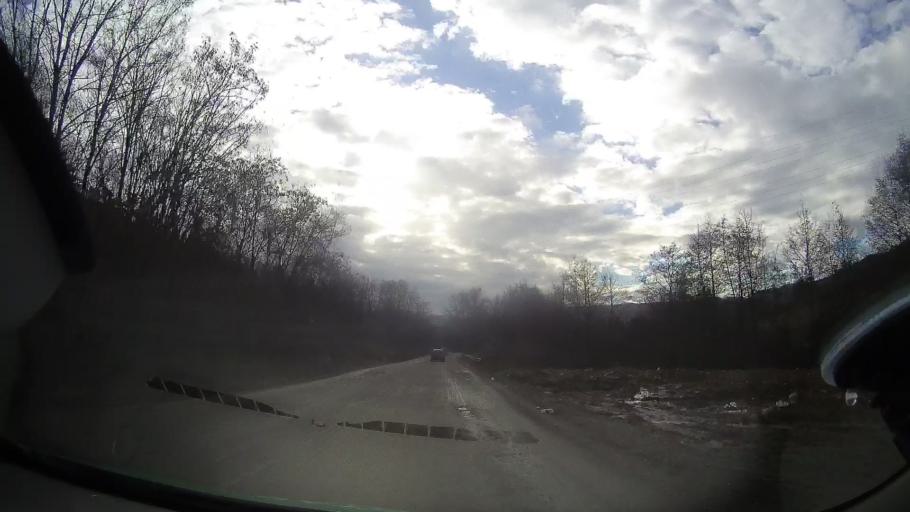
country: RO
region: Cluj
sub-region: Comuna Baisoara
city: Baisoara
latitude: 46.5831
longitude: 23.4626
